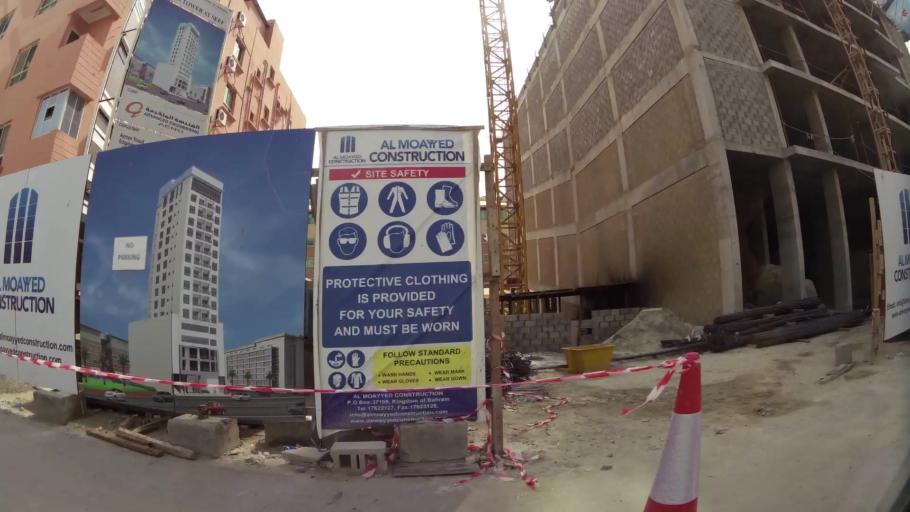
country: BH
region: Manama
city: Jidd Hafs
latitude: 26.2362
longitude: 50.5315
